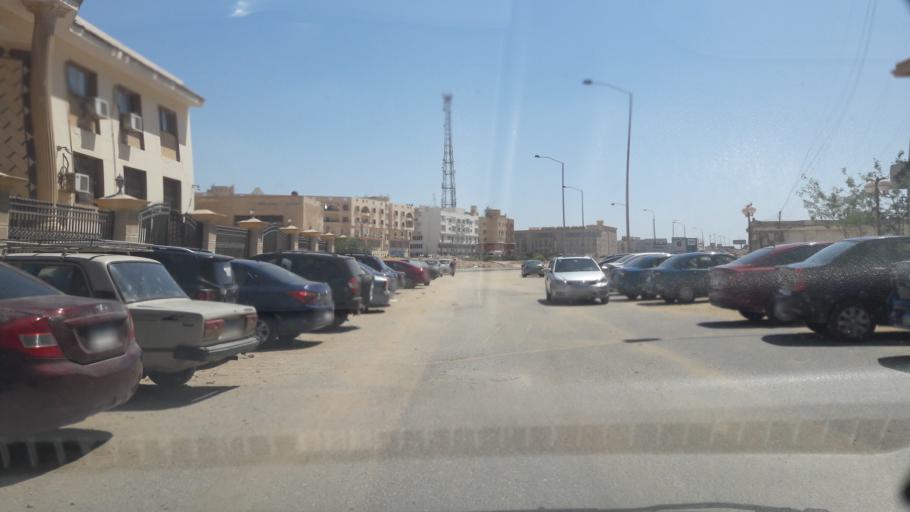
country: EG
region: Al Jizah
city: Madinat Sittah Uktubar
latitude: 29.9657
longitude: 30.9316
